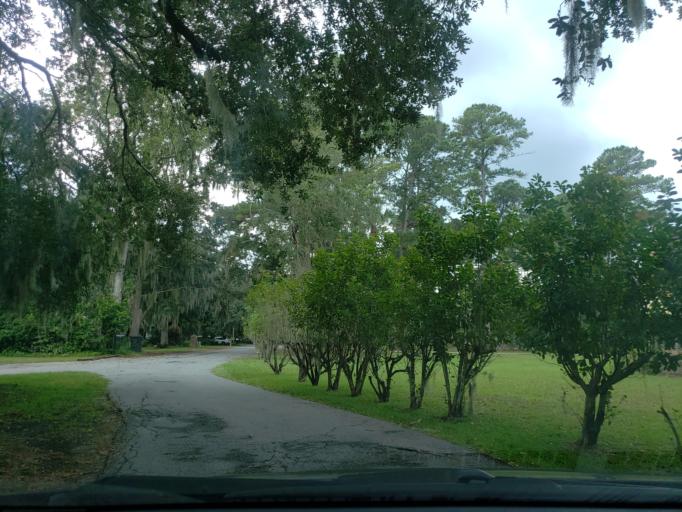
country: US
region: Georgia
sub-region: Chatham County
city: Montgomery
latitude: 31.9310
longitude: -81.0853
